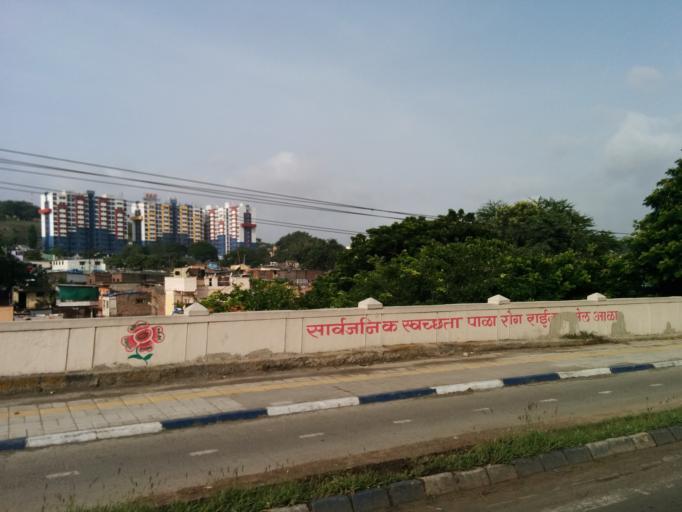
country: IN
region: Maharashtra
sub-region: Pune Division
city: Pune
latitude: 18.5057
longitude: 73.9155
